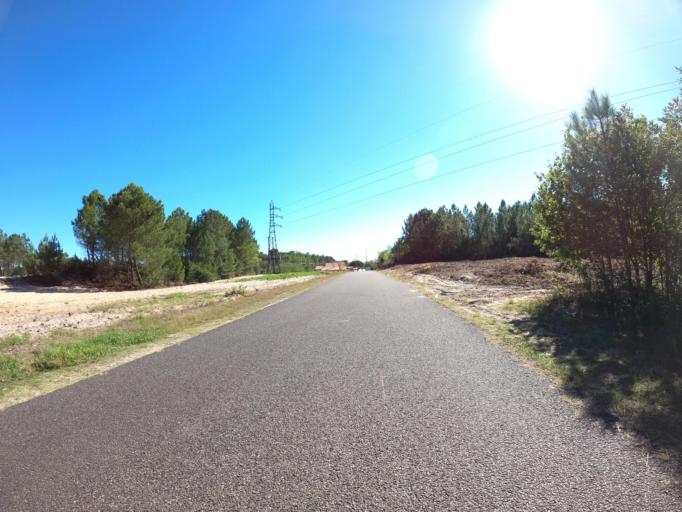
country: FR
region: Aquitaine
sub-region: Departement des Landes
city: Ychoux
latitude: 44.3354
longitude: -0.9483
